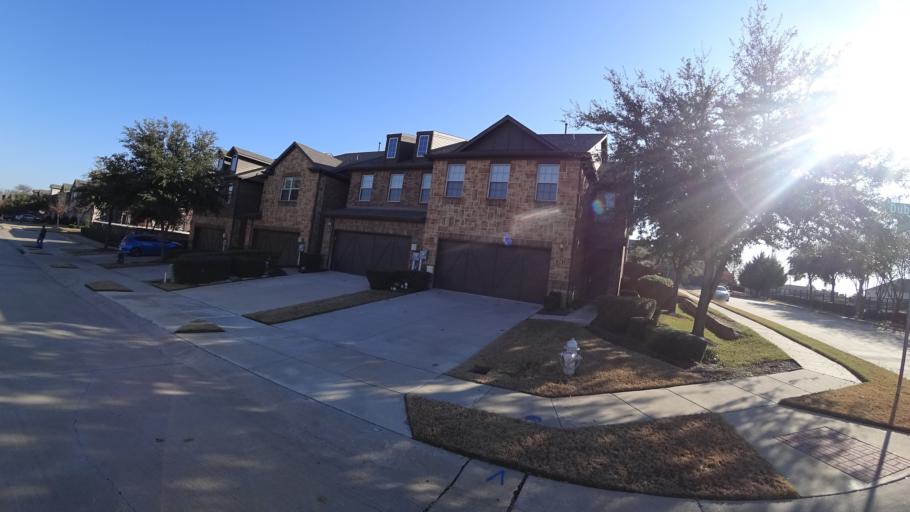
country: US
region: Texas
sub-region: Denton County
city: Lewisville
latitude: 33.0078
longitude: -96.9822
